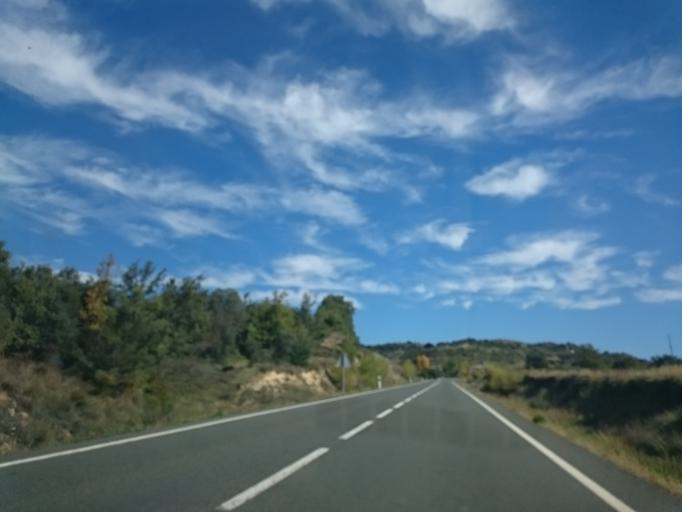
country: ES
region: Aragon
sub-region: Provincia de Huesca
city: Castigaleu
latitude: 42.1353
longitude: 0.6148
